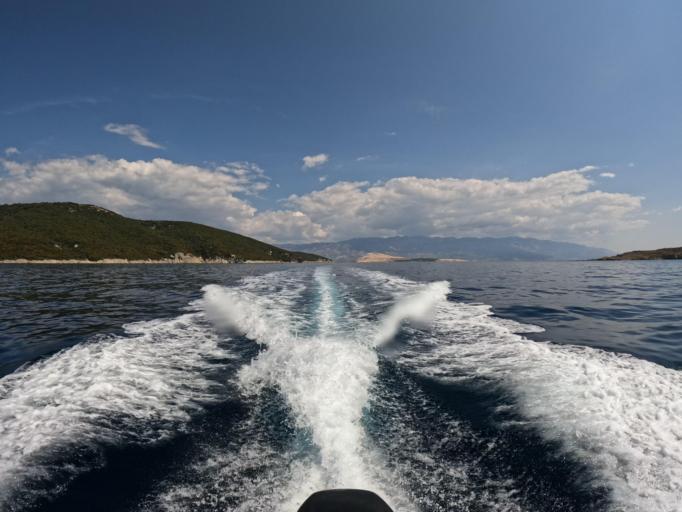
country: HR
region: Primorsko-Goranska
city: Lopar
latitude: 44.8552
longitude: 14.7463
